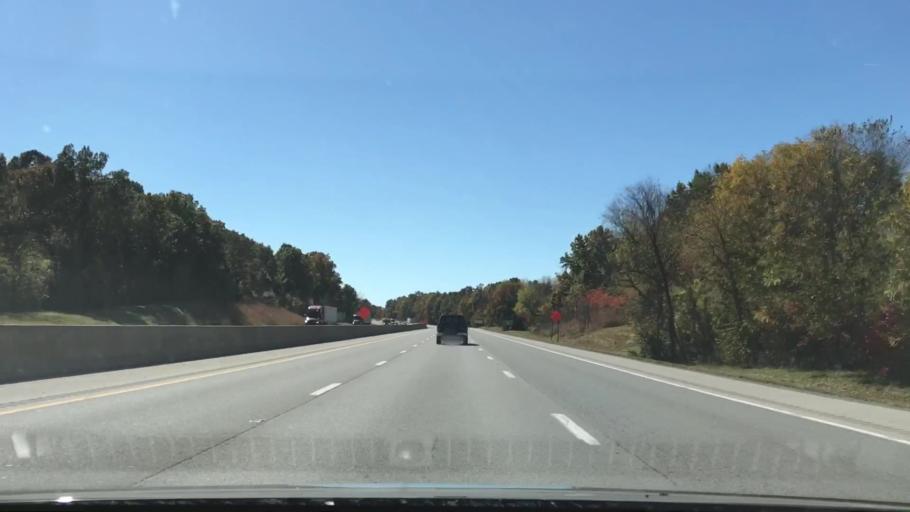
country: US
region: Kentucky
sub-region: Simpson County
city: Franklin
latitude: 36.6569
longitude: -86.5632
